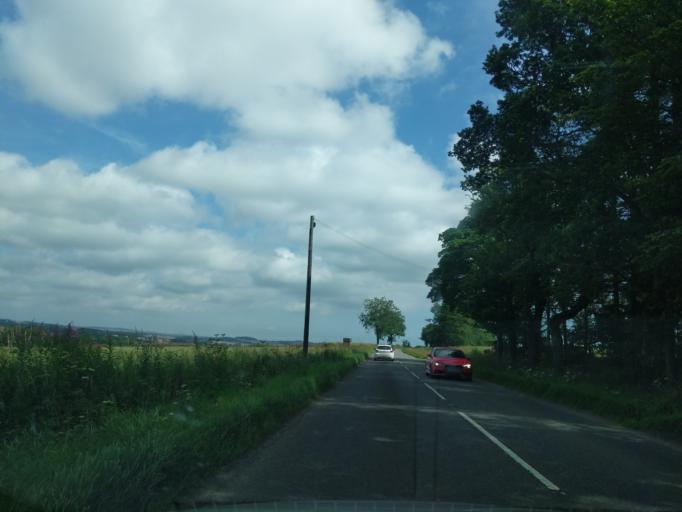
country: GB
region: Scotland
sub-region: Angus
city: Muirhead
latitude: 56.5041
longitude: -3.1234
